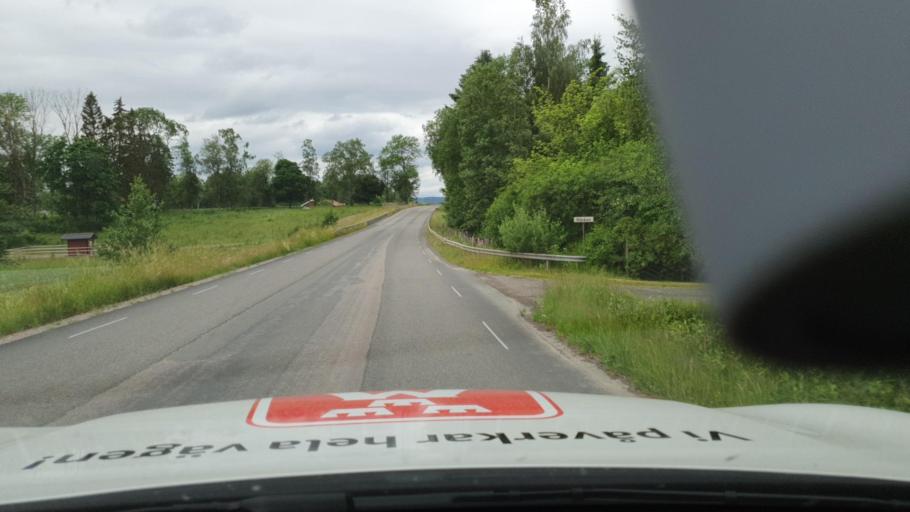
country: SE
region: Vaestra Goetaland
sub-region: Skovde Kommun
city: Skoevde
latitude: 58.3709
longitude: 13.9363
